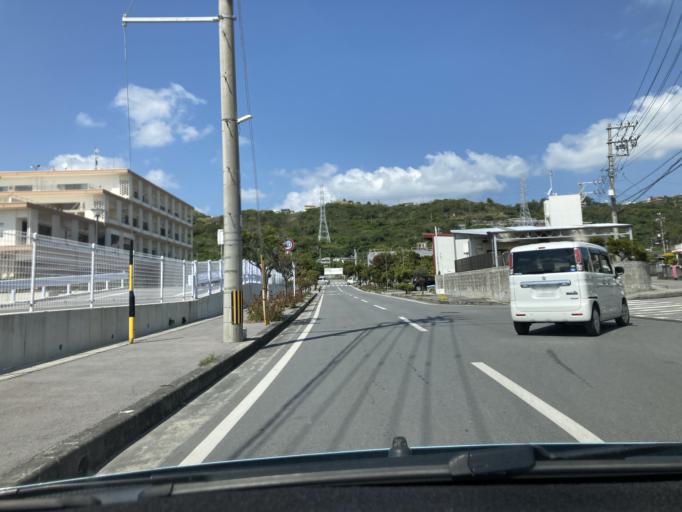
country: JP
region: Okinawa
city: Ginowan
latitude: 26.2621
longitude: 127.7905
